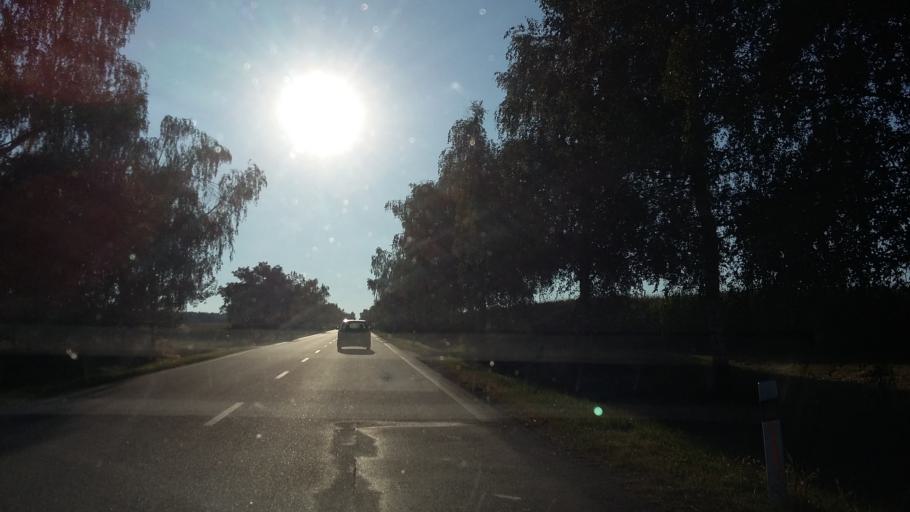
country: CZ
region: Vysocina
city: Merin
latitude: 49.4006
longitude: 15.8389
